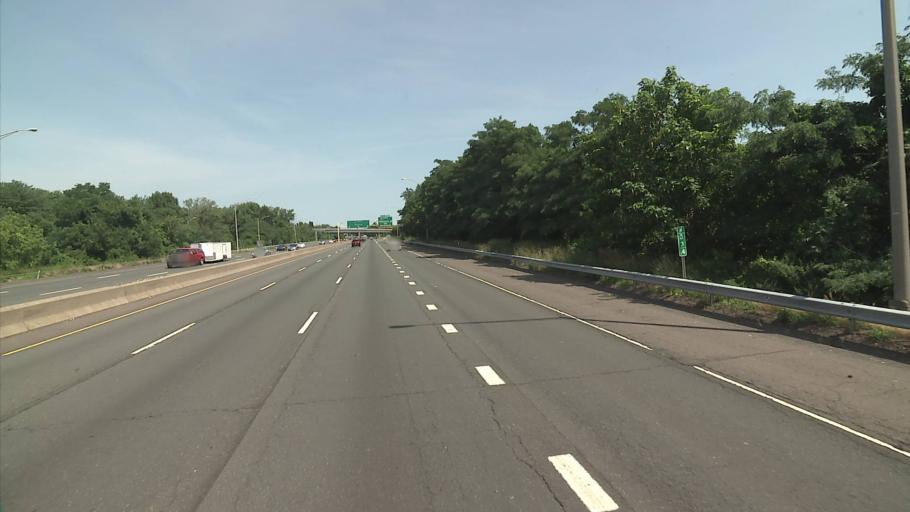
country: US
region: Connecticut
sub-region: Hartford County
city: Wethersfield
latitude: 41.7032
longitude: -72.6442
